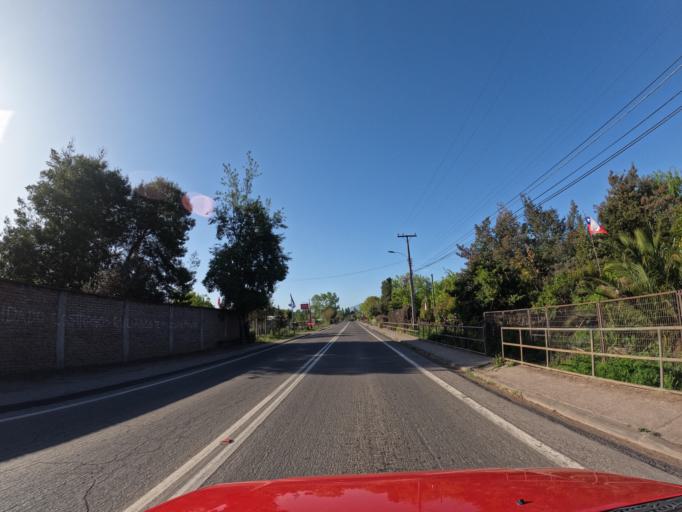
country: CL
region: Maule
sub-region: Provincia de Curico
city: Teno
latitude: -34.7535
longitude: -71.2387
